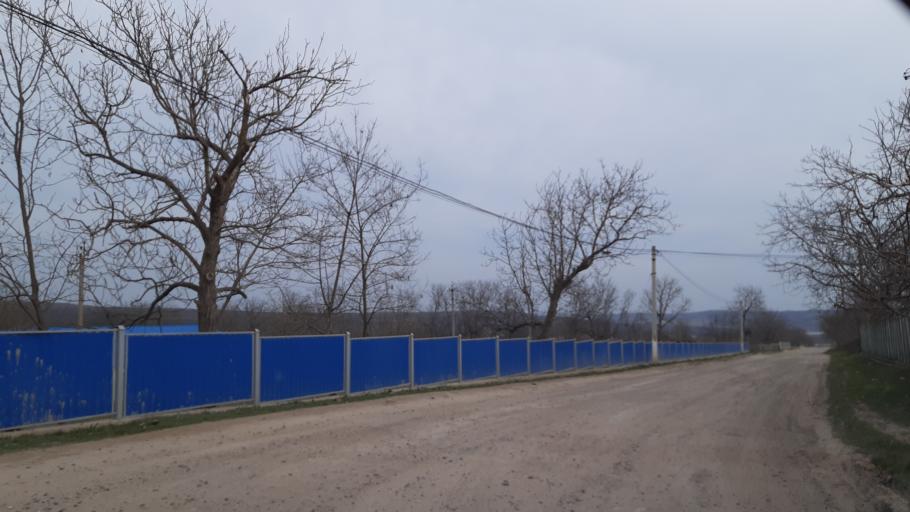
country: MD
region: Soldanesti
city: Soldanesti
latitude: 47.7116
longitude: 28.7064
